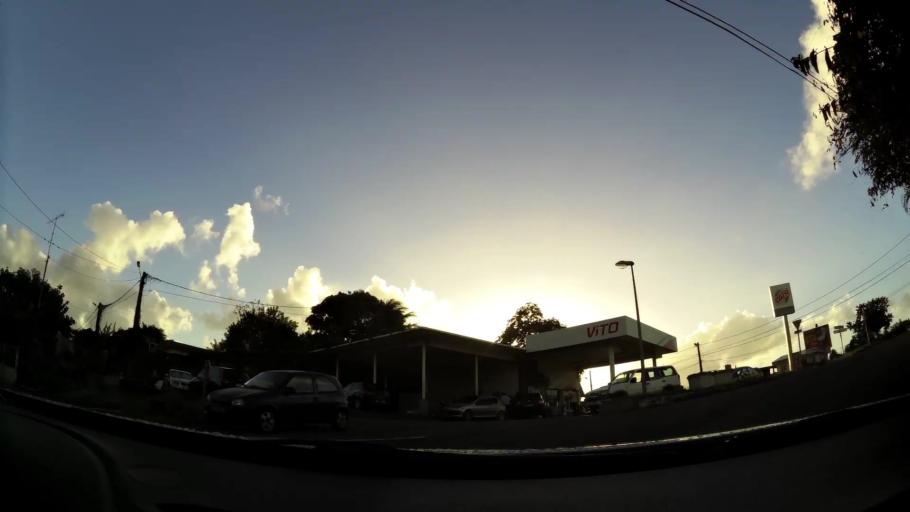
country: MQ
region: Martinique
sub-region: Martinique
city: Fort-de-France
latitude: 14.6286
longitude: -61.0720
